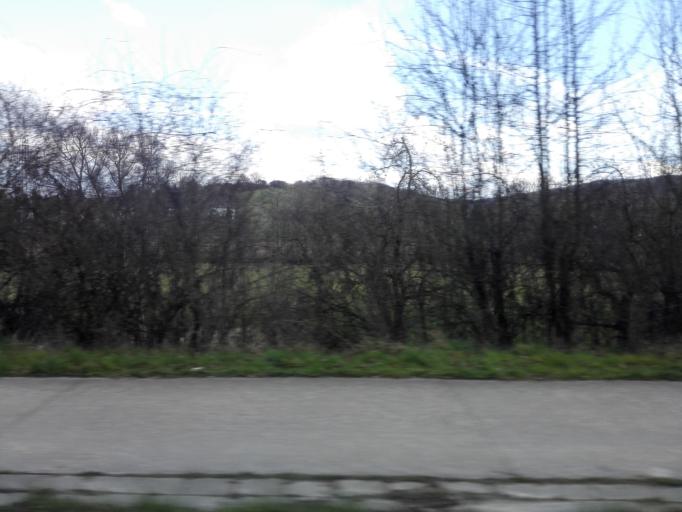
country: DE
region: Lower Saxony
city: Bad Salzdetfurth
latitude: 52.0877
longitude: 10.0313
